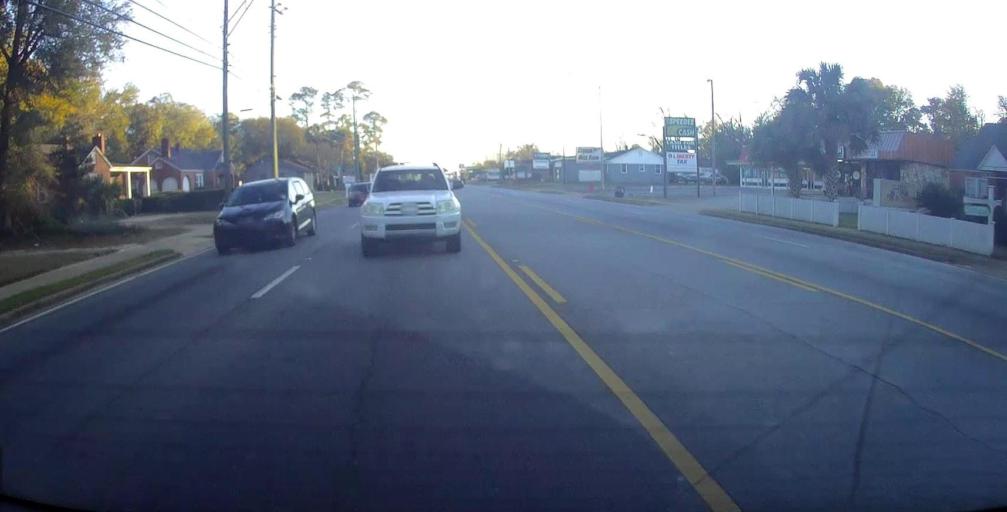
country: US
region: Georgia
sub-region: Dougherty County
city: Albany
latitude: 31.5878
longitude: -84.1762
